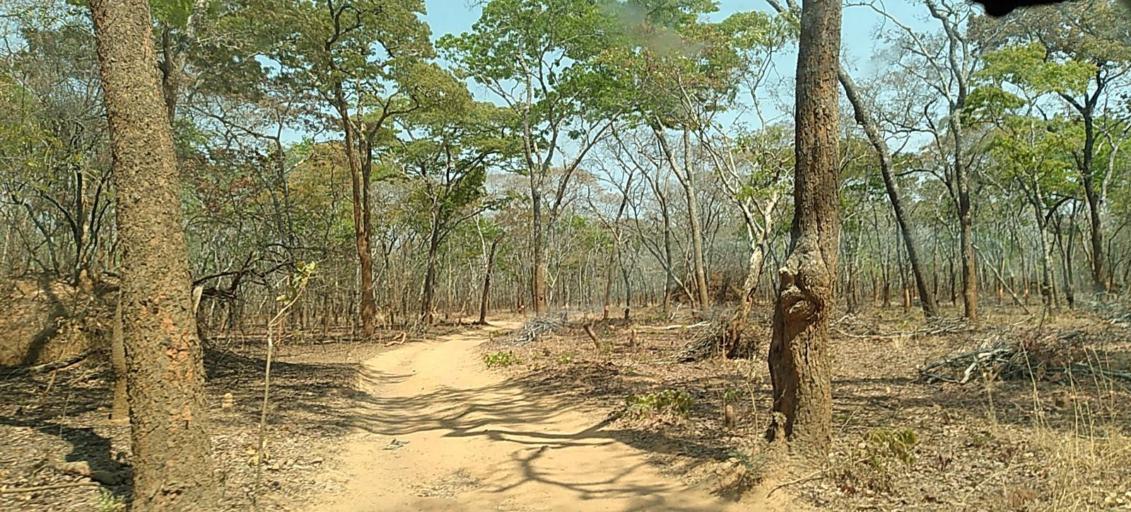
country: ZM
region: North-Western
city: Kasempa
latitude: -13.3930
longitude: 25.6045
